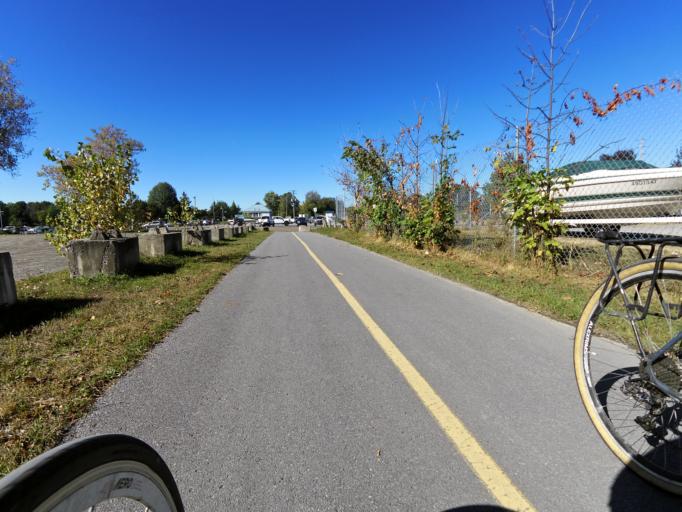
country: CA
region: Quebec
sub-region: Outaouais
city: Gatineau
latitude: 45.4770
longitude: -75.6389
